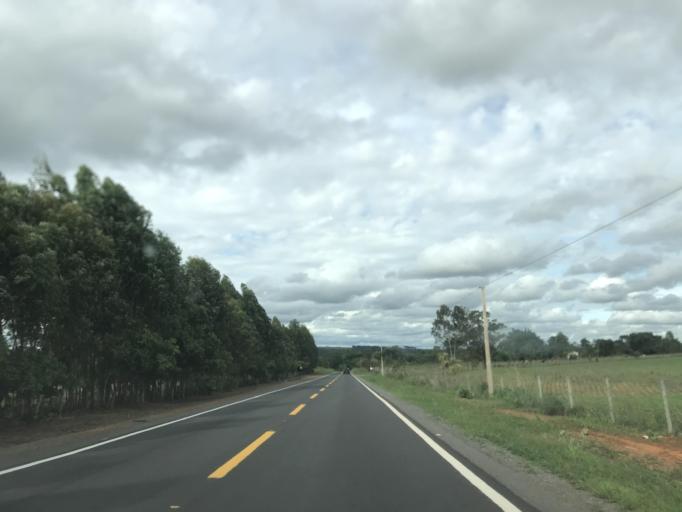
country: BR
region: Goias
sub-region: Bela Vista De Goias
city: Bela Vista de Goias
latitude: -17.1776
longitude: -48.6856
